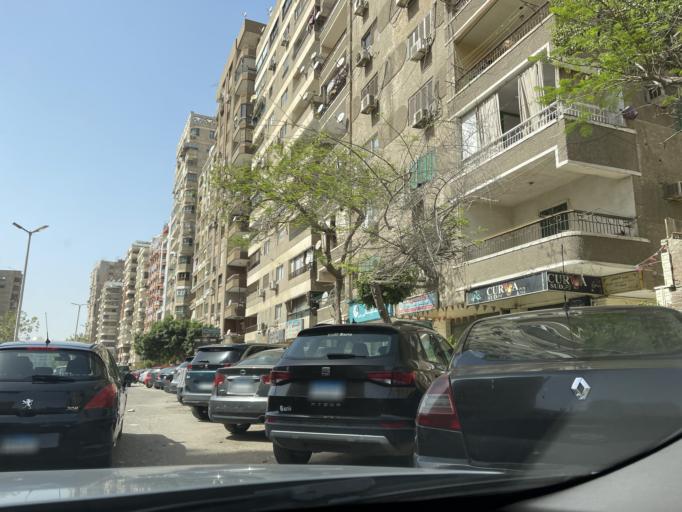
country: EG
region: Muhafazat al Qahirah
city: Cairo
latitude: 30.0662
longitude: 31.3566
